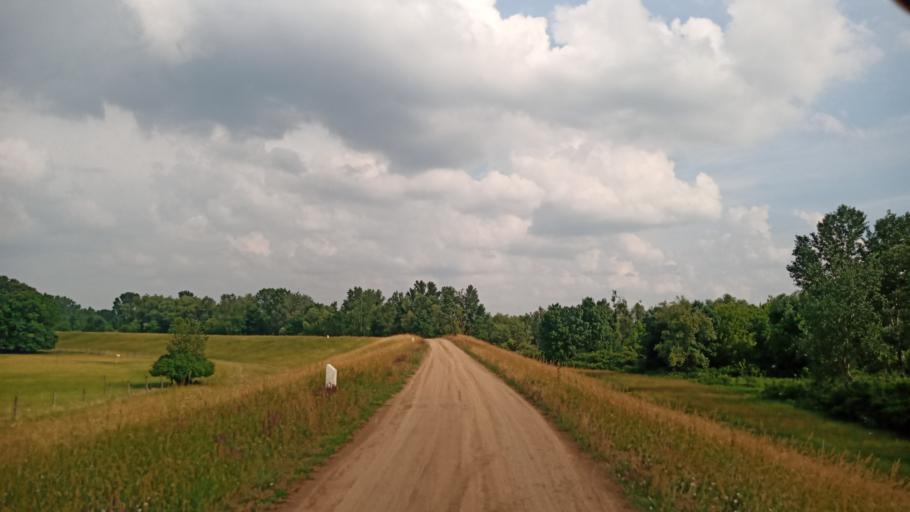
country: HU
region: Bekes
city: Gyula
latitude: 46.7056
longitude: 21.3054
